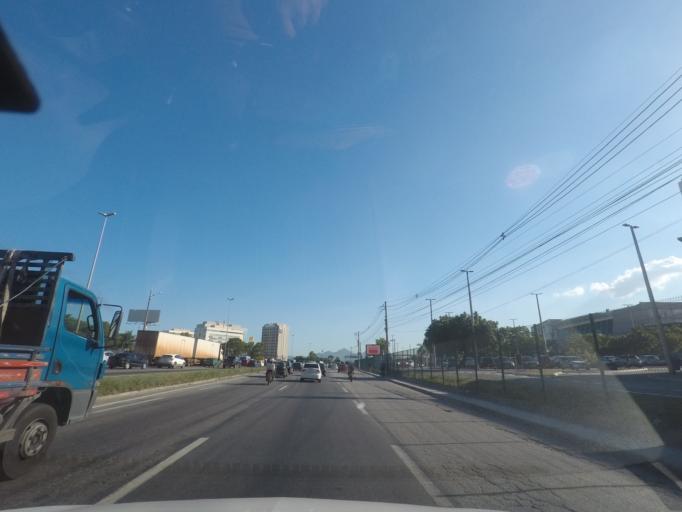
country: BR
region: Rio de Janeiro
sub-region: Duque De Caxias
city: Duque de Caxias
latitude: -22.7861
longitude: -43.2856
